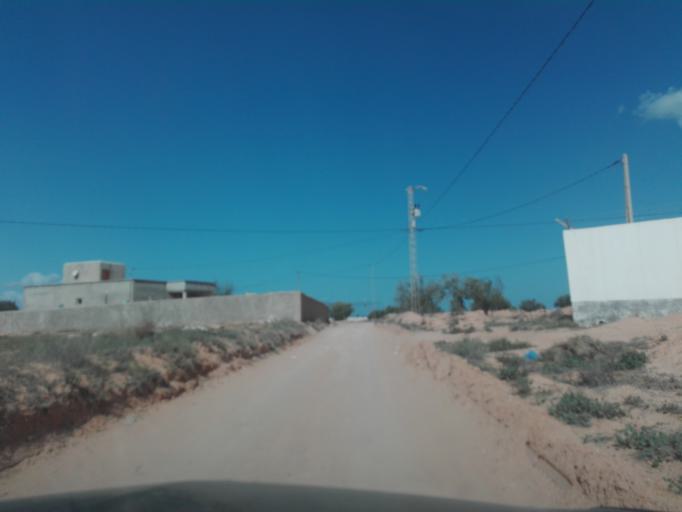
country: TN
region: Madanin
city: Bin Qirdan
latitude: 33.1689
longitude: 11.1969
